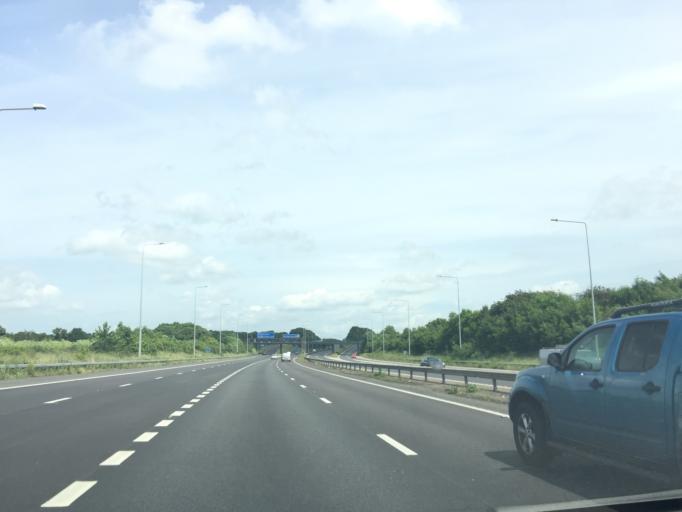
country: GB
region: England
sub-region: Kent
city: Rainham
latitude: 51.3340
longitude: 0.5764
